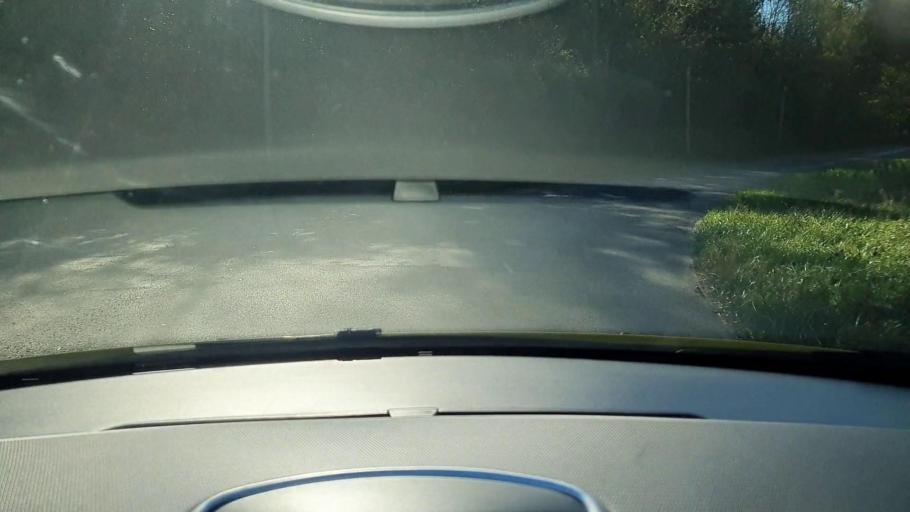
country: FR
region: Languedoc-Roussillon
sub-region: Departement du Gard
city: Le Vigan
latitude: 43.9876
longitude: 3.4972
